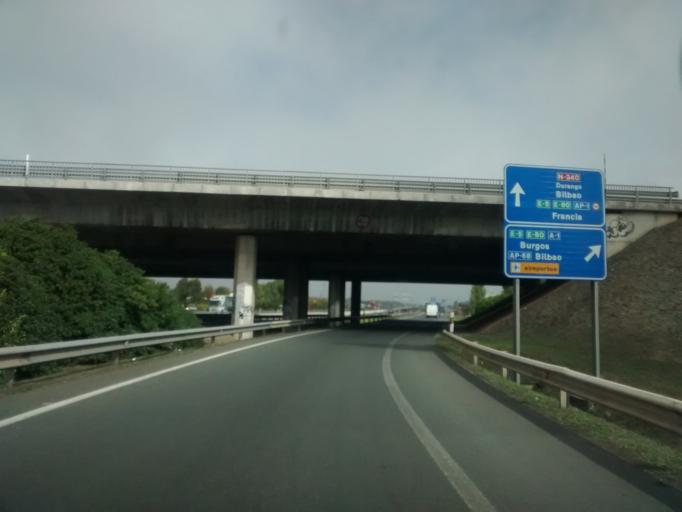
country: ES
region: Basque Country
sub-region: Provincia de Alava
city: Gasteiz / Vitoria
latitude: 42.8803
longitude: -2.6559
